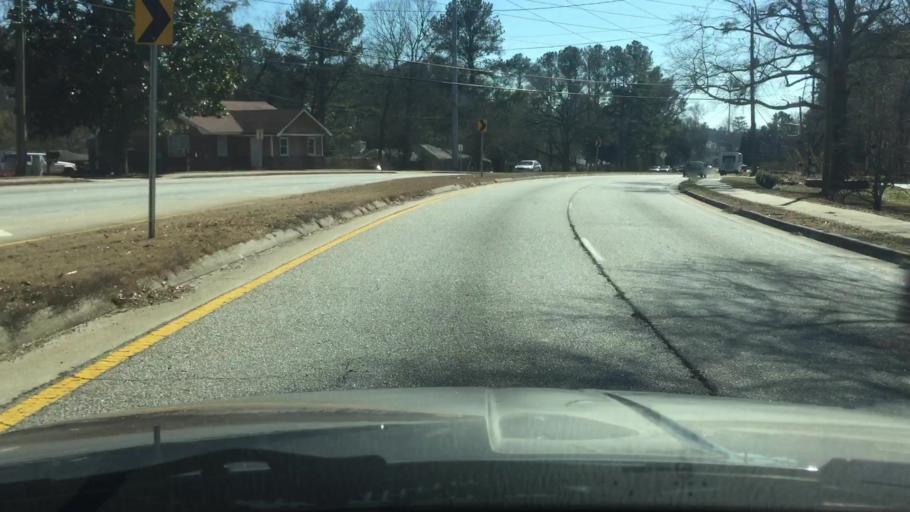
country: US
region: Georgia
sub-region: DeKalb County
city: Redan
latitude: 33.7446
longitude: -84.1960
